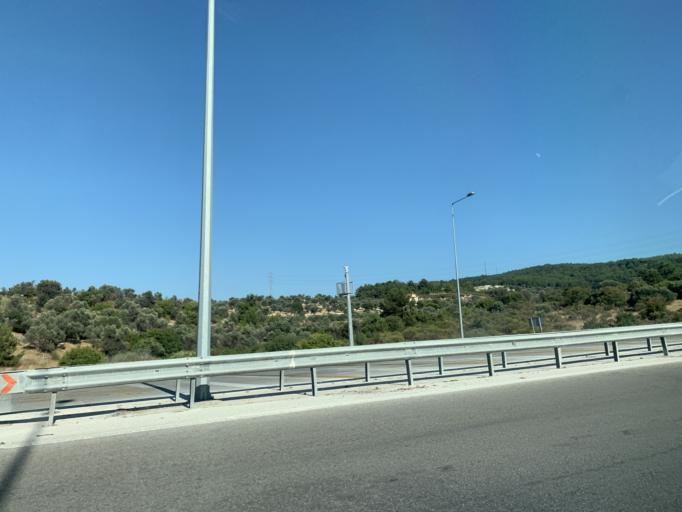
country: TR
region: Izmir
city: Urla
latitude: 38.3223
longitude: 26.7818
